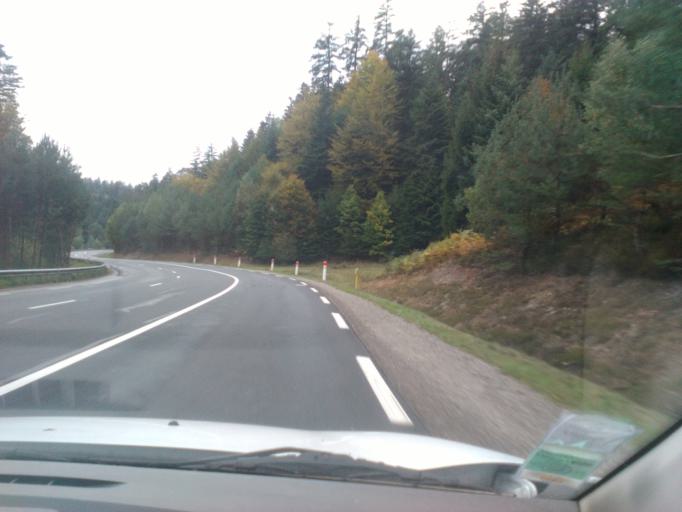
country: FR
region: Lorraine
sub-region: Departement des Vosges
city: Jeanmenil
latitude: 48.3254
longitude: 6.7747
